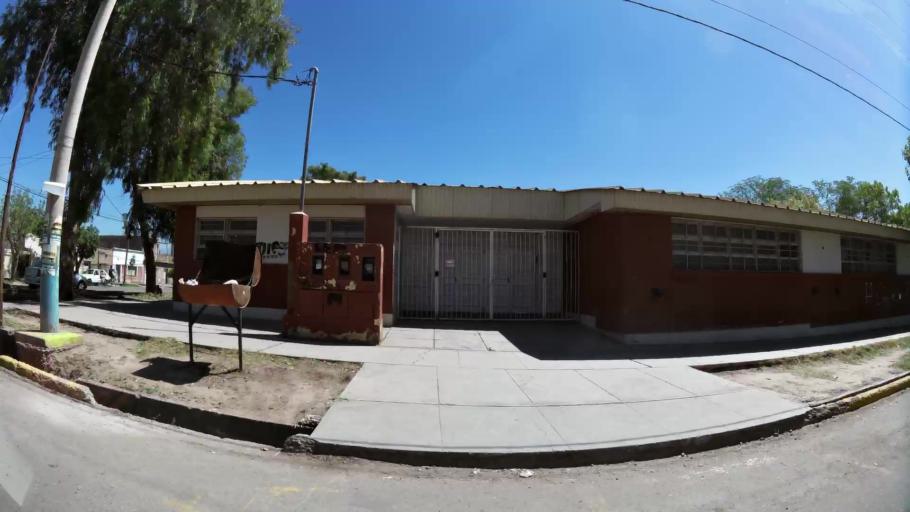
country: AR
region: Mendoza
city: Villa Nueva
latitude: -32.8805
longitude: -68.7879
